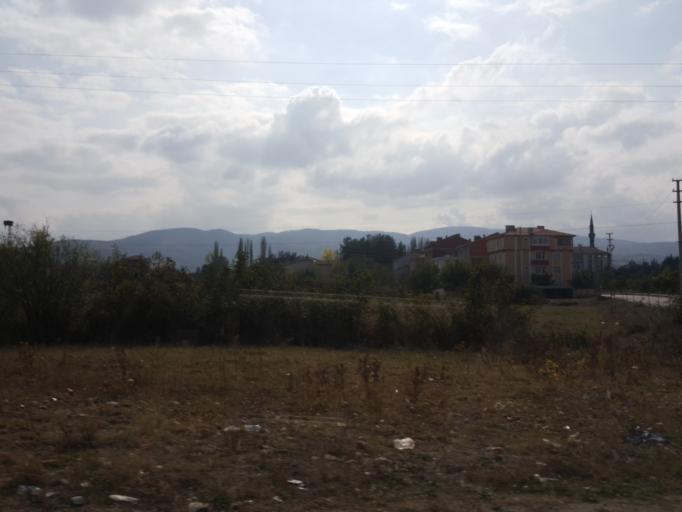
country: TR
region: Sinop
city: Sarayduzu
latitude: 41.3333
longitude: 34.8506
